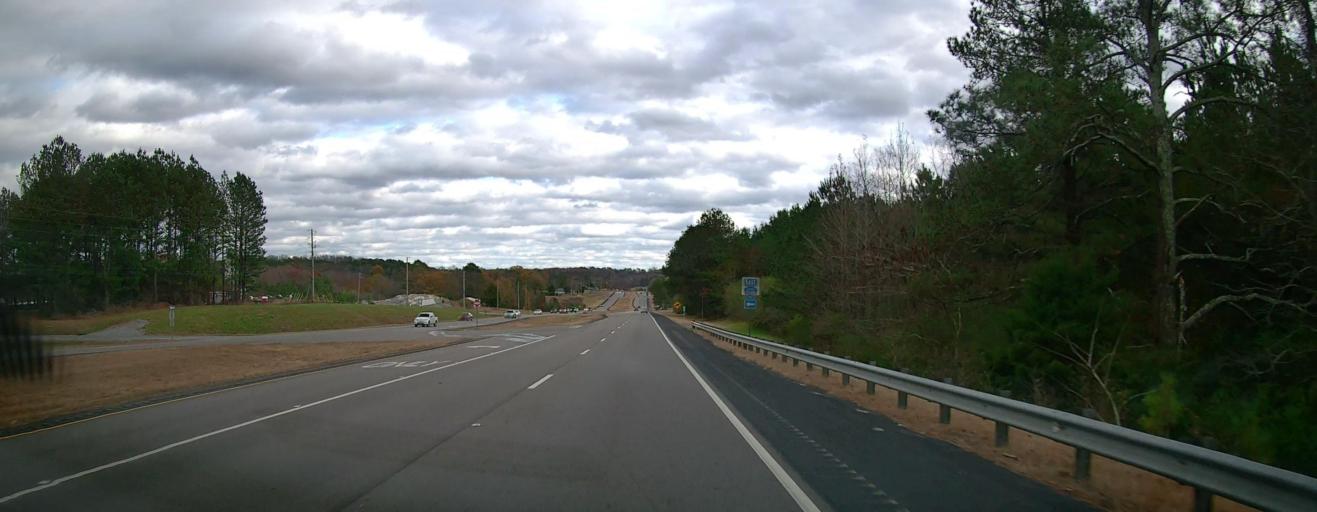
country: US
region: Alabama
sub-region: Cullman County
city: Cullman
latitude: 34.2363
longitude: -86.9345
